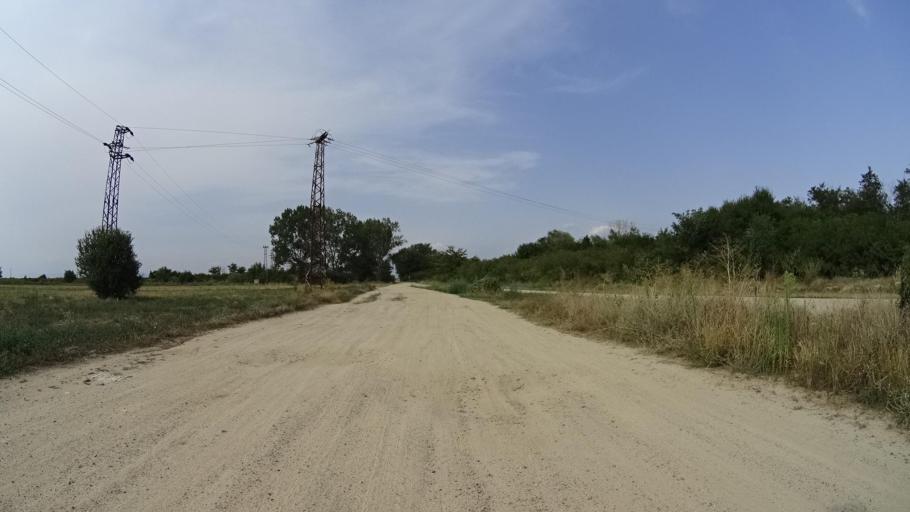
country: BG
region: Plovdiv
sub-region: Obshtina Kaloyanovo
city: Kaloyanovo
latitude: 42.3038
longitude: 24.7992
